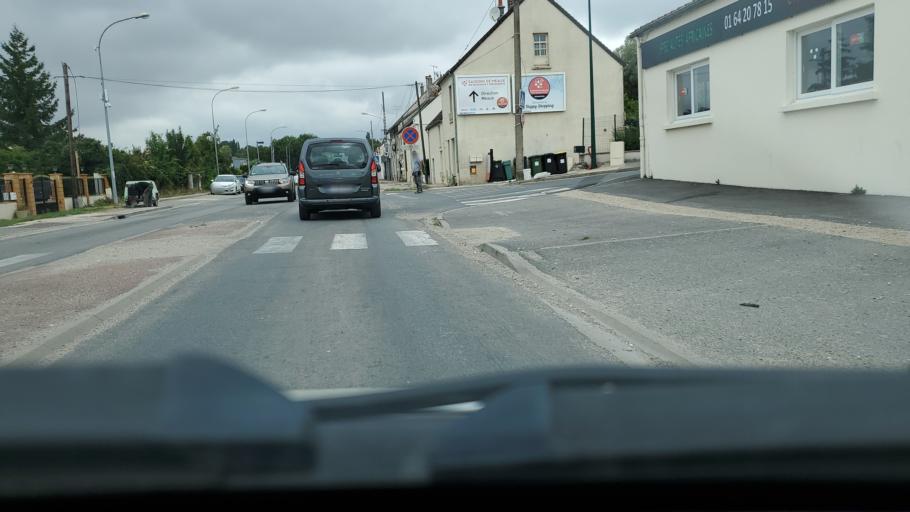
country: FR
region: Ile-de-France
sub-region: Departement de Seine-et-Marne
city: Mouroux
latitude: 48.8216
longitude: 3.0460
